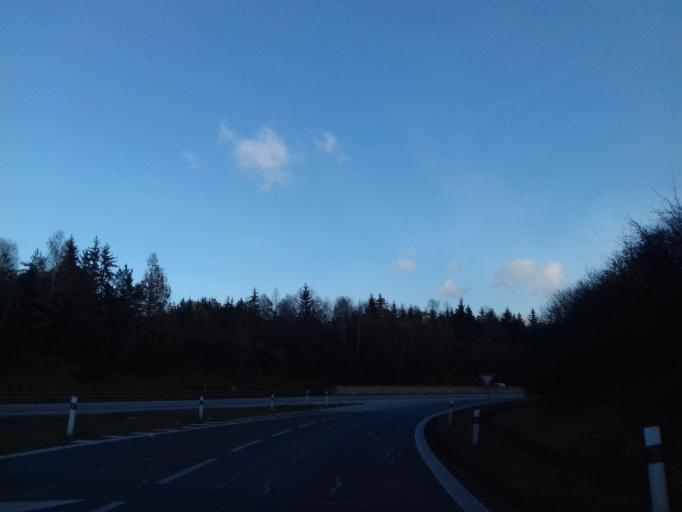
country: CZ
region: Plzensky
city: Vejprnice
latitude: 49.7071
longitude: 13.2837
